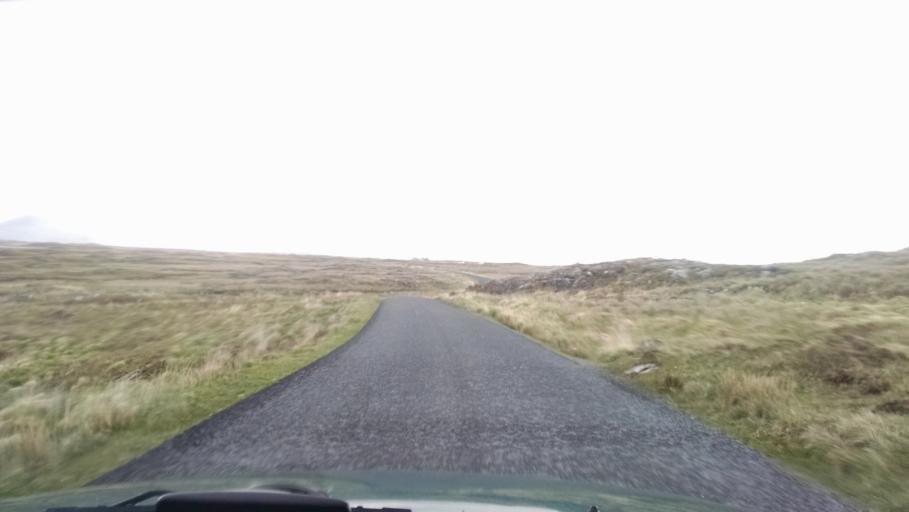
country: IE
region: Connaught
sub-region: County Galway
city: Clifden
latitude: 53.4406
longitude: -9.9225
